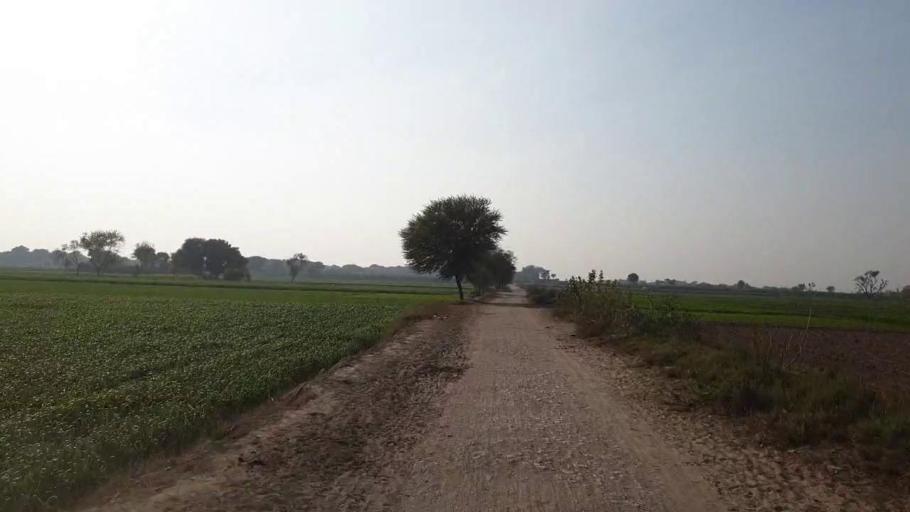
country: PK
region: Sindh
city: Matiari
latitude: 25.5995
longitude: 68.5946
